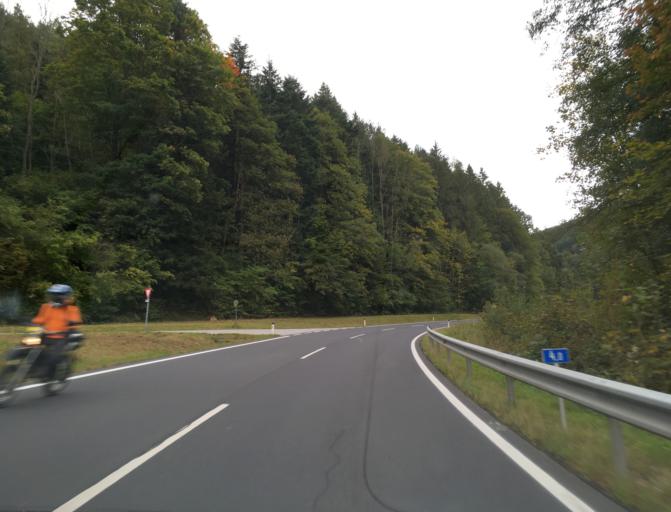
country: AT
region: Lower Austria
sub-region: Politischer Bezirk Neunkirchen
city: Edlitz
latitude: 47.5828
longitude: 16.1454
